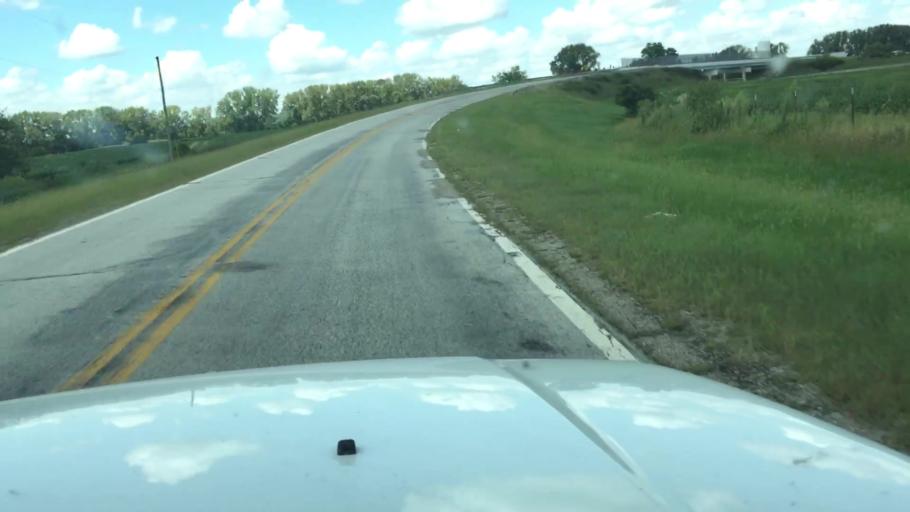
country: US
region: Ohio
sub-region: Madison County
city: Choctaw Lake
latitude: 39.9354
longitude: -83.5689
